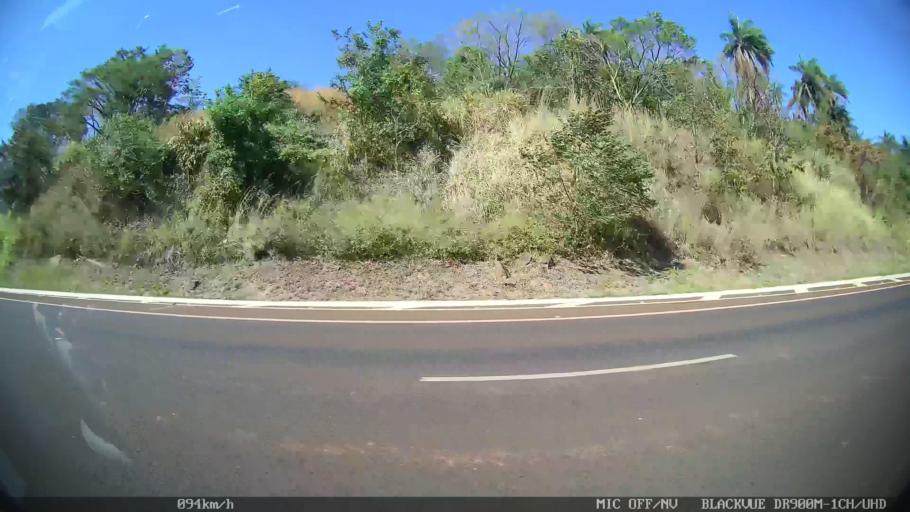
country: BR
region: Sao Paulo
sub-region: Franca
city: Franca
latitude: -20.6061
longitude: -47.4517
